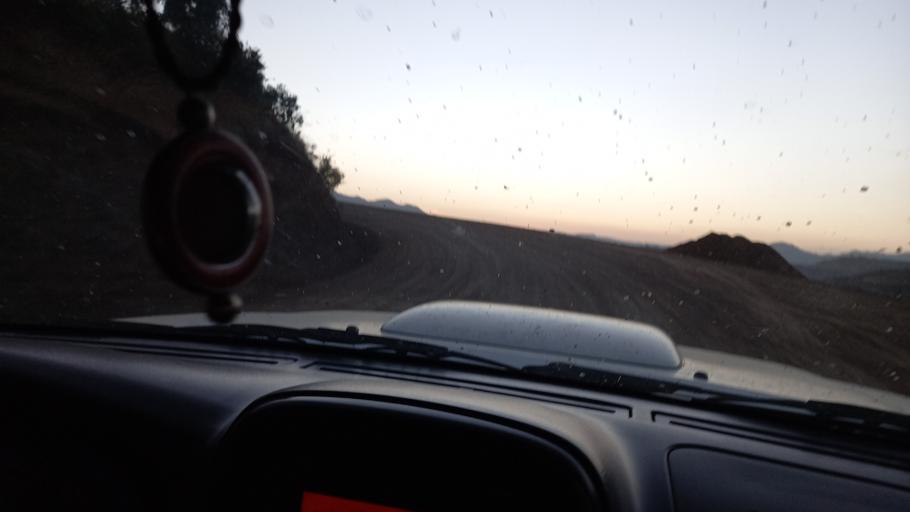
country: ET
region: Amhara
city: Debark'
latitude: 13.0340
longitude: 38.0545
